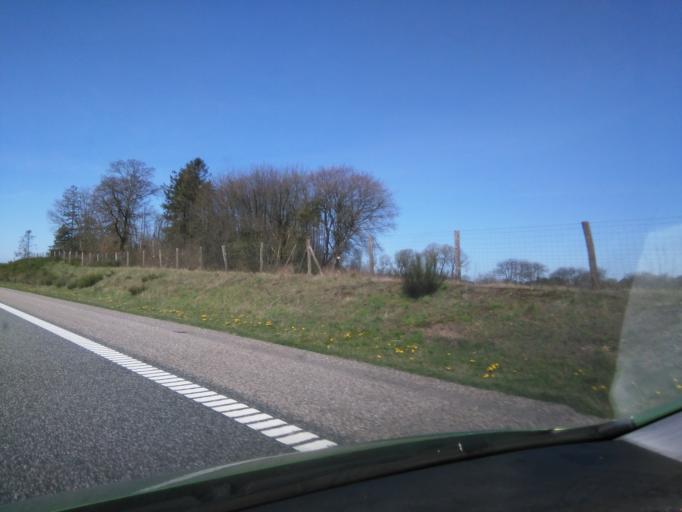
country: DK
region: South Denmark
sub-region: Vejle Kommune
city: Jelling
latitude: 55.8361
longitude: 9.3723
